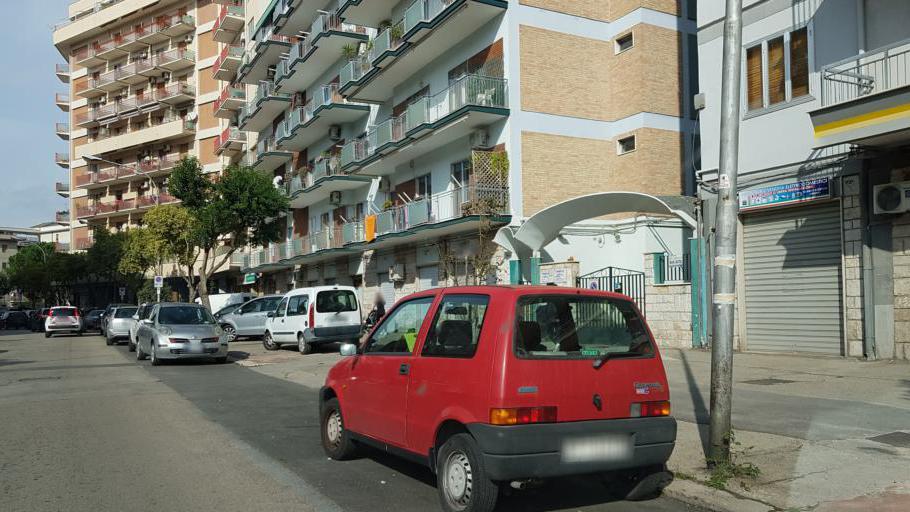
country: IT
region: Apulia
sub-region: Provincia di Foggia
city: Foggia
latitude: 41.4545
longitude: 15.5602
